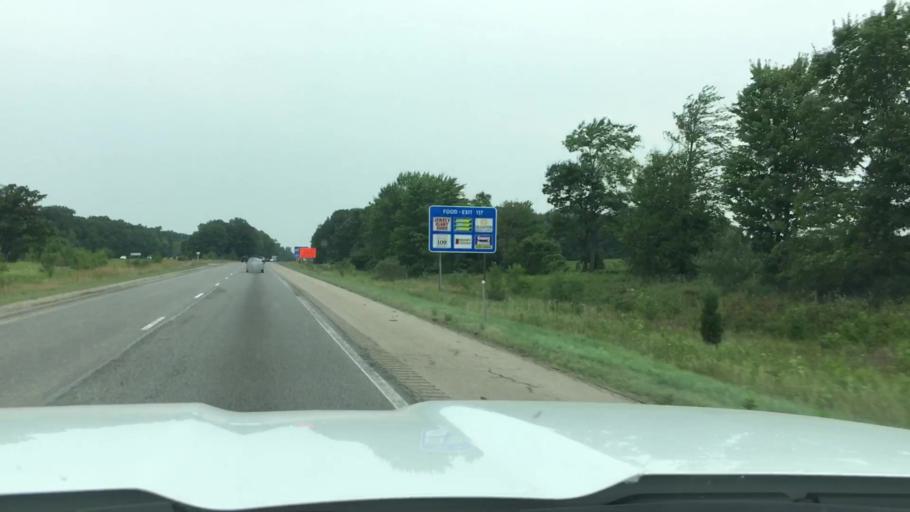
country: US
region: Michigan
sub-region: Ingham County
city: Williamston
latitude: 42.6659
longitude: -84.2650
